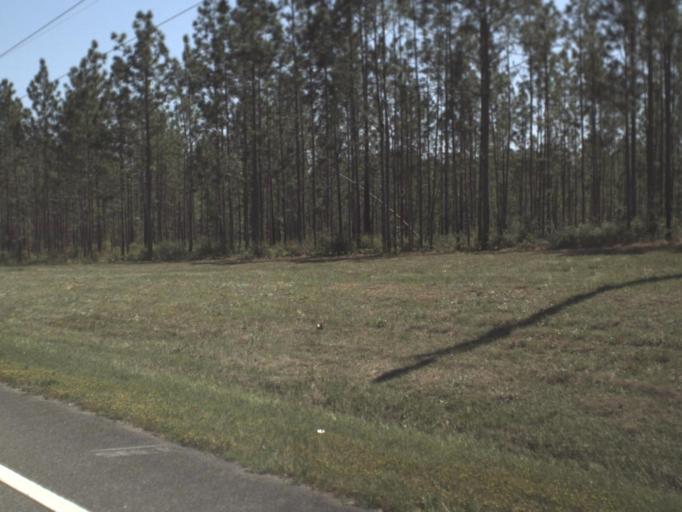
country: US
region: Florida
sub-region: Santa Rosa County
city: Point Baker
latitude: 30.8858
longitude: -86.9662
